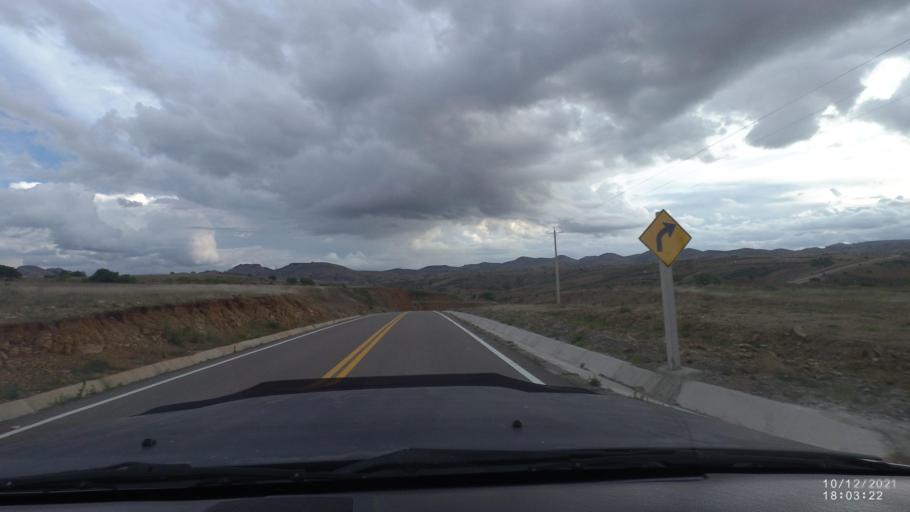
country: BO
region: Cochabamba
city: Cliza
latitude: -17.7590
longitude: -65.9187
